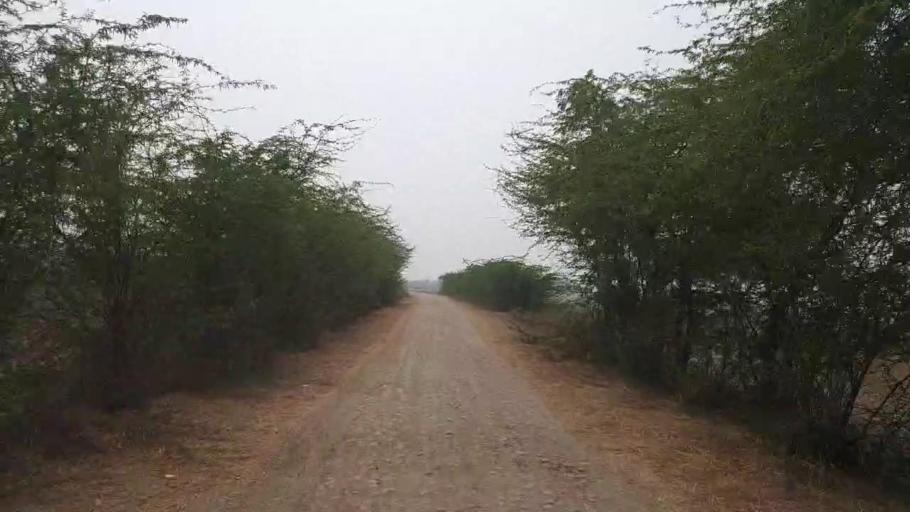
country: PK
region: Sindh
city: Kario
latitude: 24.6496
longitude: 68.6402
